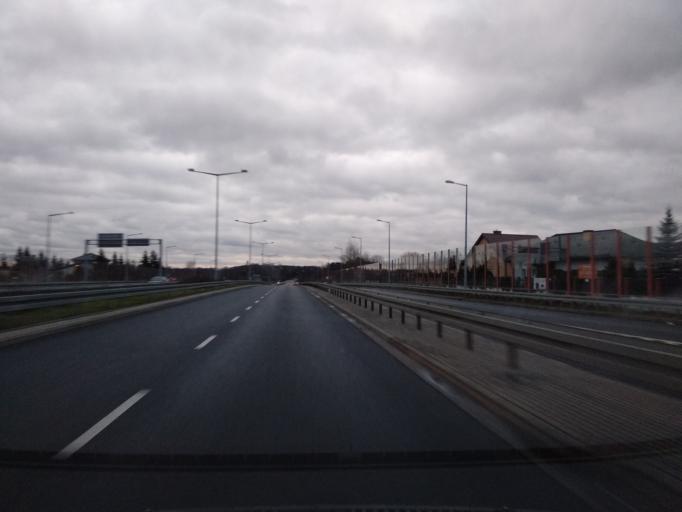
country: PL
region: Greater Poland Voivodeship
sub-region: Powiat koninski
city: Stare Miasto
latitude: 52.1800
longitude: 18.2227
